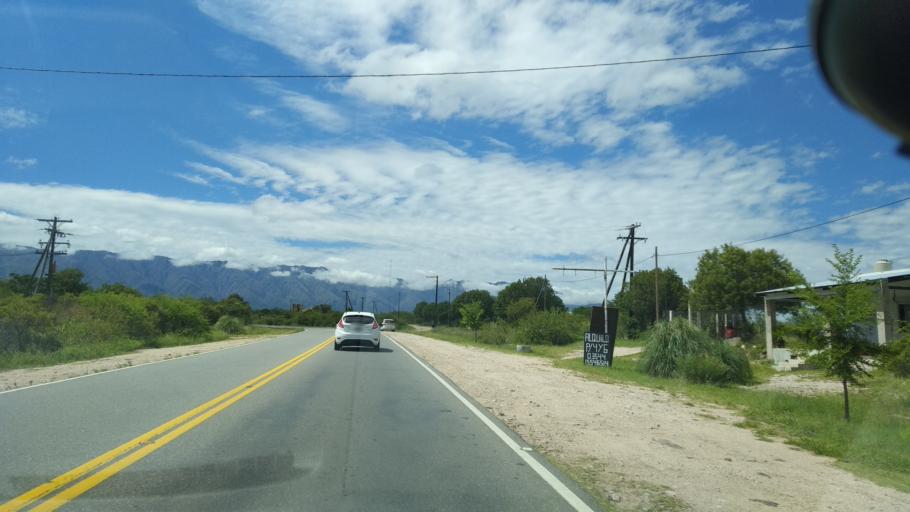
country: AR
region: Cordoba
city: Mina Clavero
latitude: -31.7620
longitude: -64.9709
